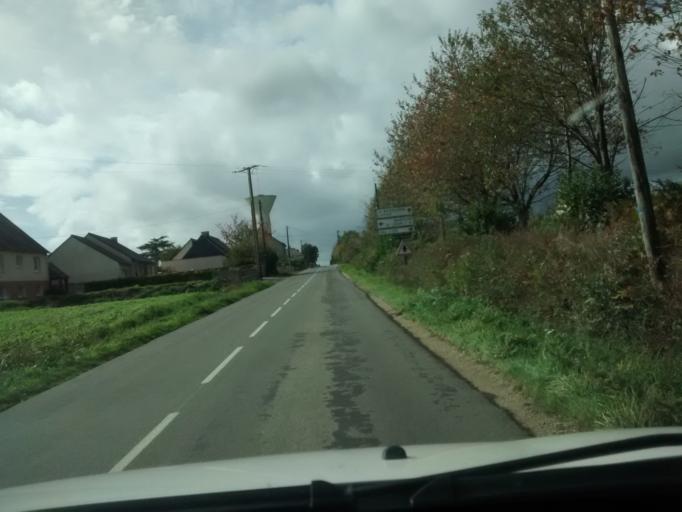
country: FR
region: Brittany
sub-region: Departement d'Ille-et-Vilaine
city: Saint-Didier
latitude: 48.1487
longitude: -1.3378
